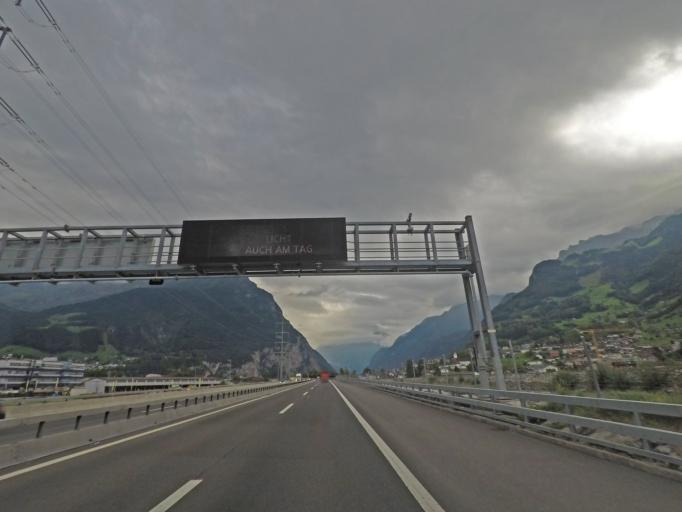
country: CH
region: Uri
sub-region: Uri
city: Attinghausen
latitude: 46.8693
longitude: 8.6297
